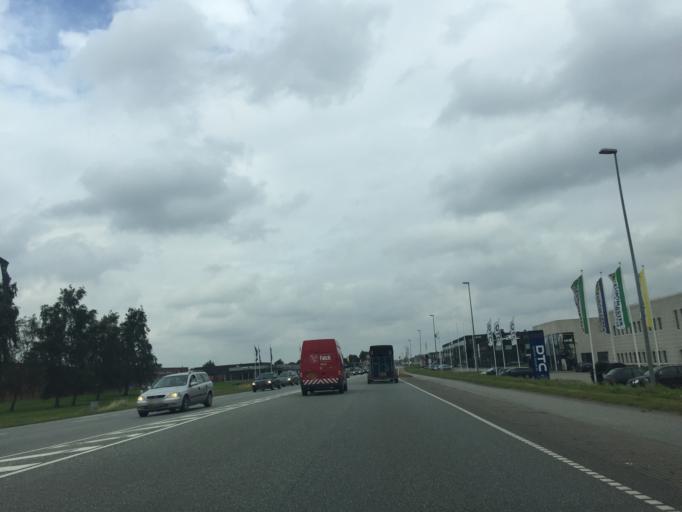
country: DK
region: Central Jutland
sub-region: Randers Kommune
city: Randers
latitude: 56.4345
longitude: 10.0527
